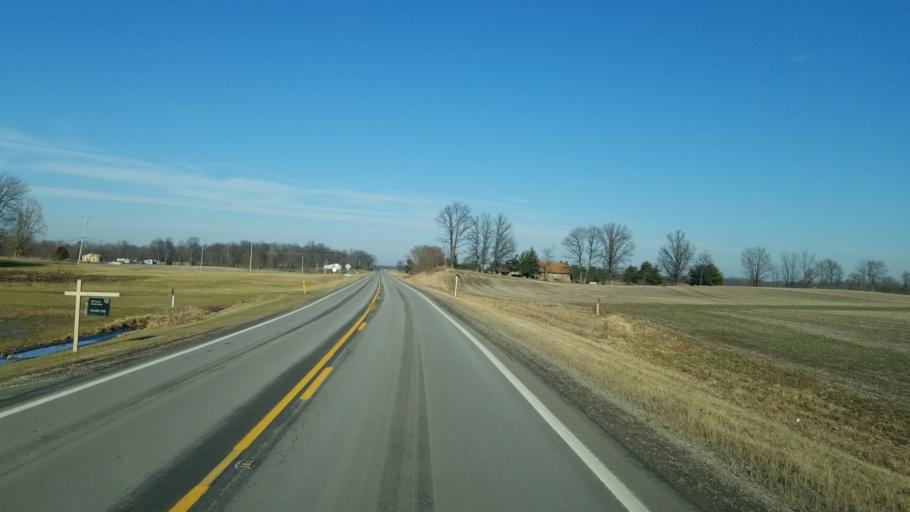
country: US
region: Ohio
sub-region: Huron County
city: Norwalk
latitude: 41.1817
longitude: -82.6396
